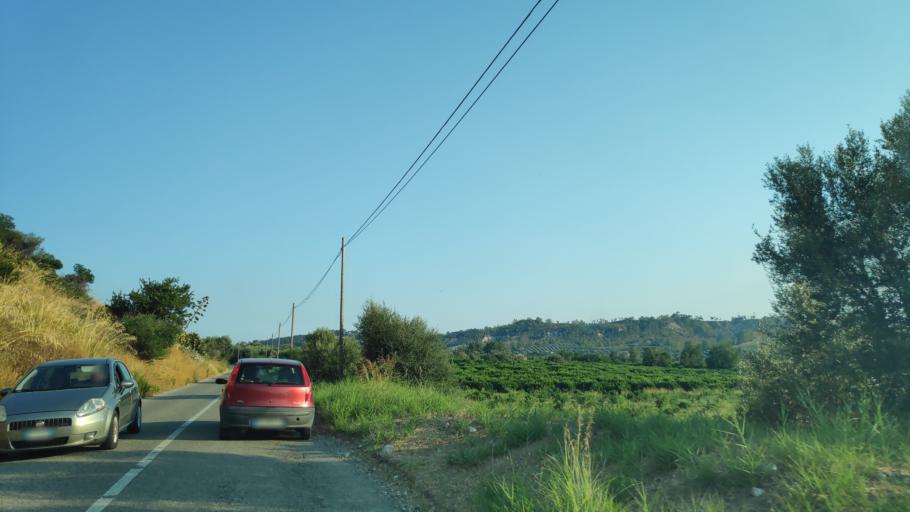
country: IT
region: Calabria
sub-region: Provincia di Reggio Calabria
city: Caulonia
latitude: 38.3782
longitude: 16.4400
